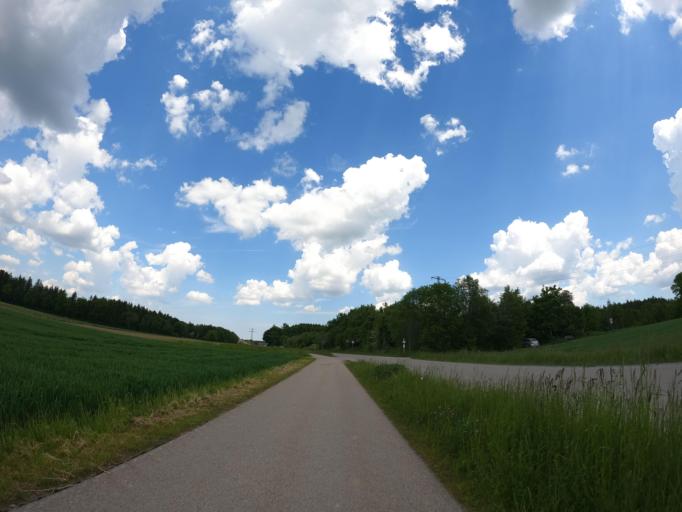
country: DE
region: Bavaria
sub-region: Upper Bavaria
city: Sauerlach
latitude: 47.9861
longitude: 11.6582
